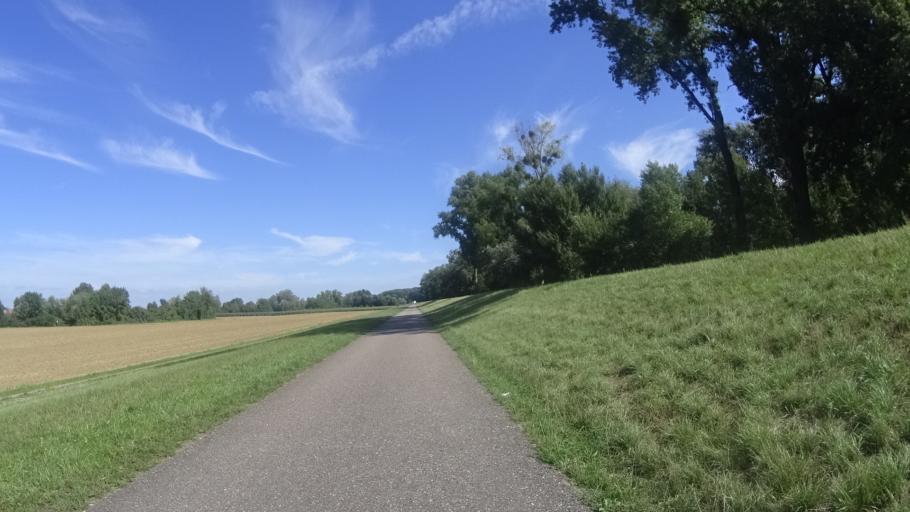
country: DE
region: Rheinland-Pfalz
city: Leimersheim
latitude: 49.1149
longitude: 8.3536
